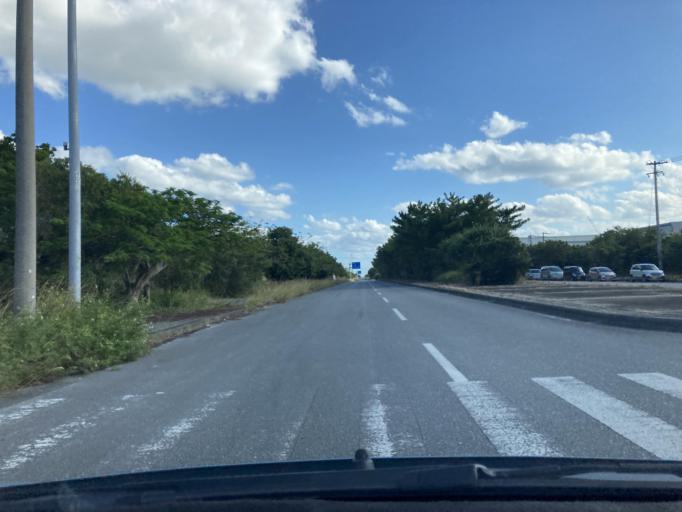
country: JP
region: Okinawa
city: Katsuren-haebaru
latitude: 26.3394
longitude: 127.8601
